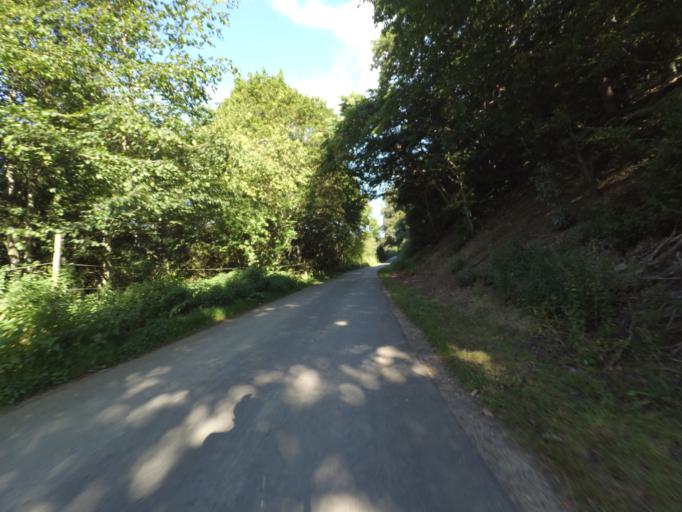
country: DE
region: Rheinland-Pfalz
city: Daun
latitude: 50.1892
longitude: 6.8158
